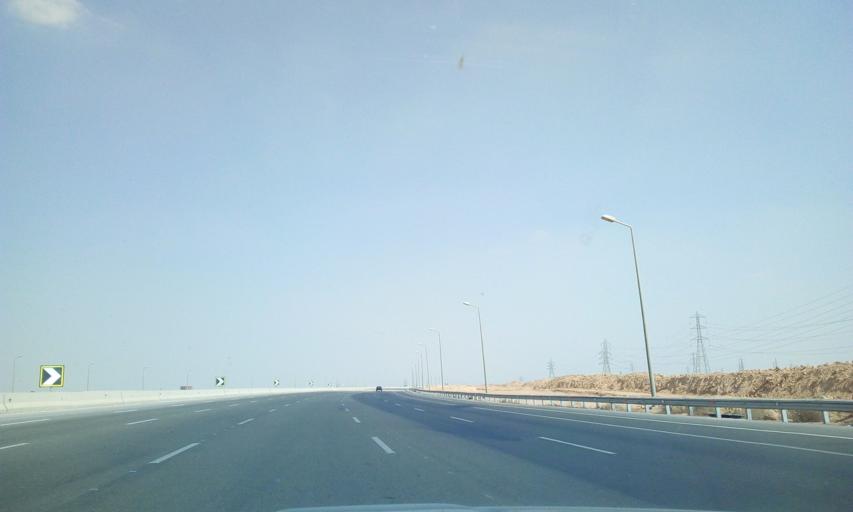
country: EG
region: Muhafazat al Qahirah
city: Halwan
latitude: 29.9246
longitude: 31.6092
